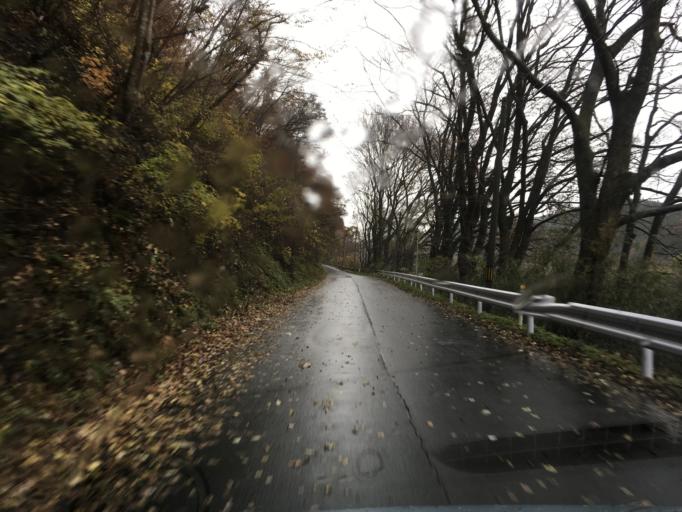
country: JP
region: Iwate
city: Ichinoseki
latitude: 38.8164
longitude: 141.2534
